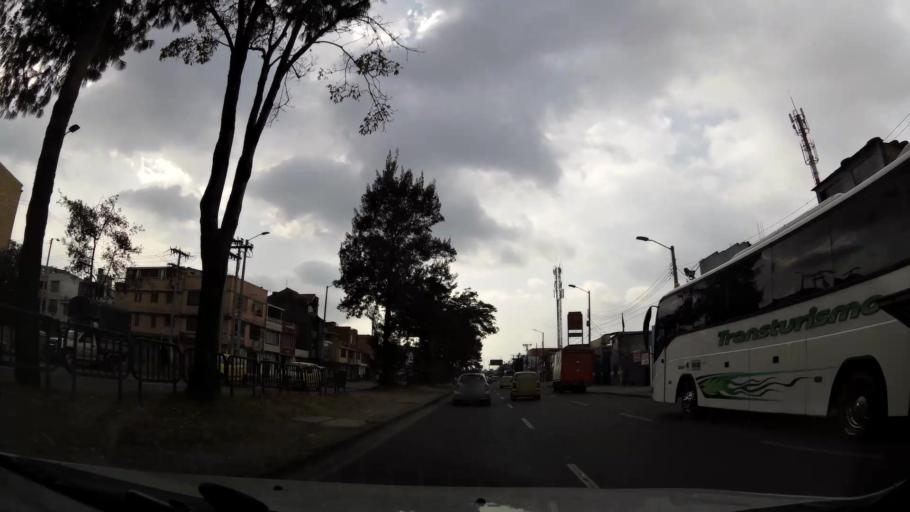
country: CO
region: Bogota D.C.
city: Bogota
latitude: 4.5904
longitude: -74.1250
